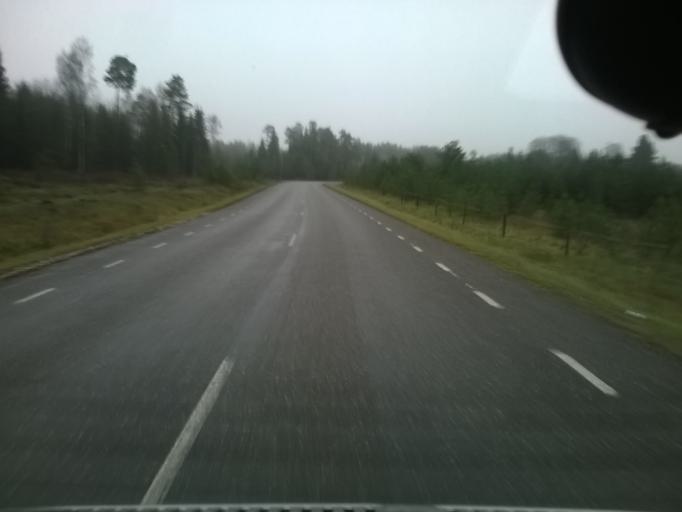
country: EE
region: Raplamaa
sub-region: Kohila vald
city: Kohila
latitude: 59.1455
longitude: 24.6063
